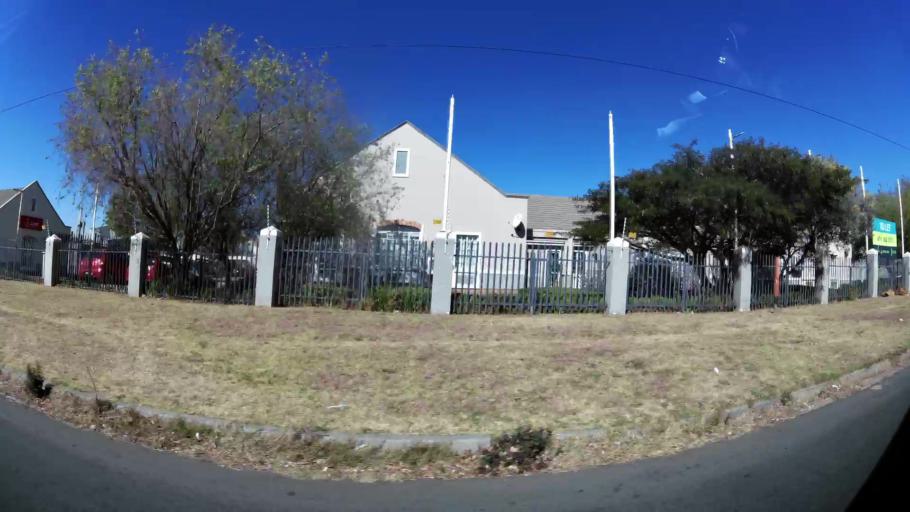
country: ZA
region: Gauteng
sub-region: City of Johannesburg Metropolitan Municipality
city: Roodepoort
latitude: -26.1681
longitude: 27.9329
